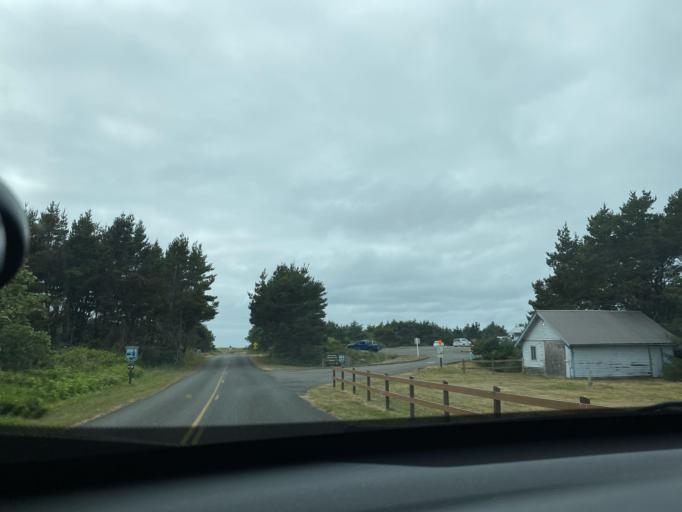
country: US
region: Washington
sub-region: Grays Harbor County
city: Ocean Shores
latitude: 47.1142
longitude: -124.1768
